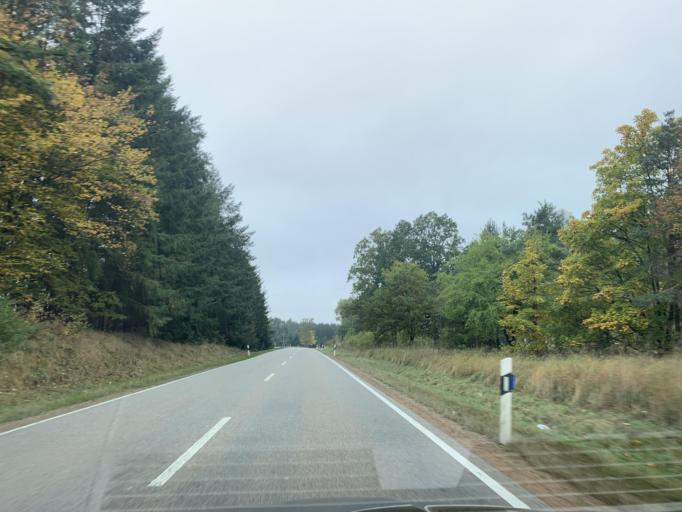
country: DE
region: Bavaria
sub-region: Upper Palatinate
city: Nabburg
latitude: 49.4517
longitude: 12.2242
